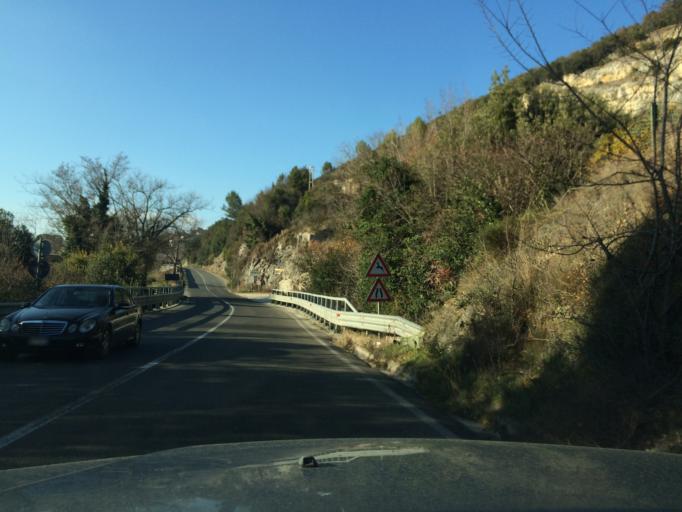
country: IT
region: Umbria
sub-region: Provincia di Terni
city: Fornole
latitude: 42.5413
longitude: 12.4652
